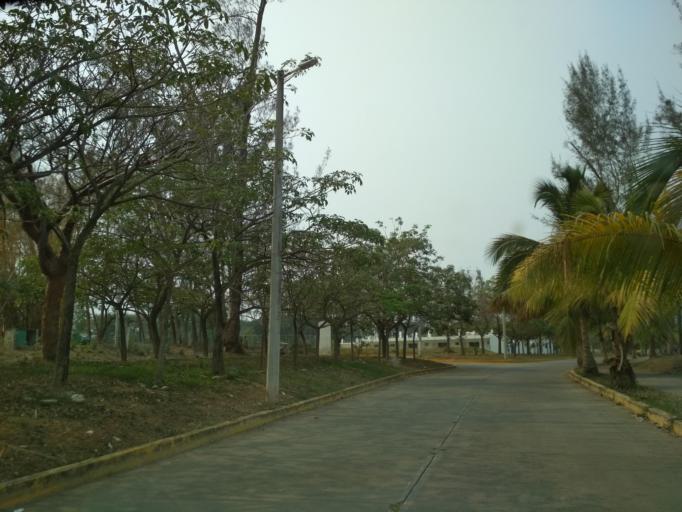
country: MX
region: Veracruz
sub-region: Veracruz
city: Las Amapolas
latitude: 19.1479
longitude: -96.2238
